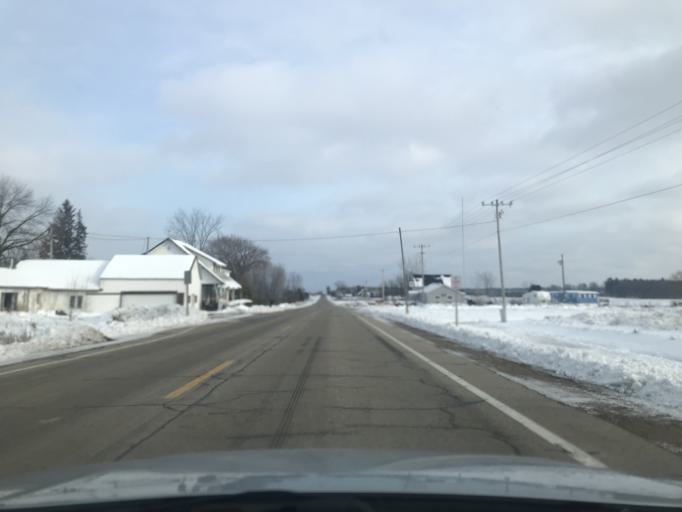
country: US
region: Wisconsin
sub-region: Oconto County
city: Oconto
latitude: 44.8927
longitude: -87.9597
